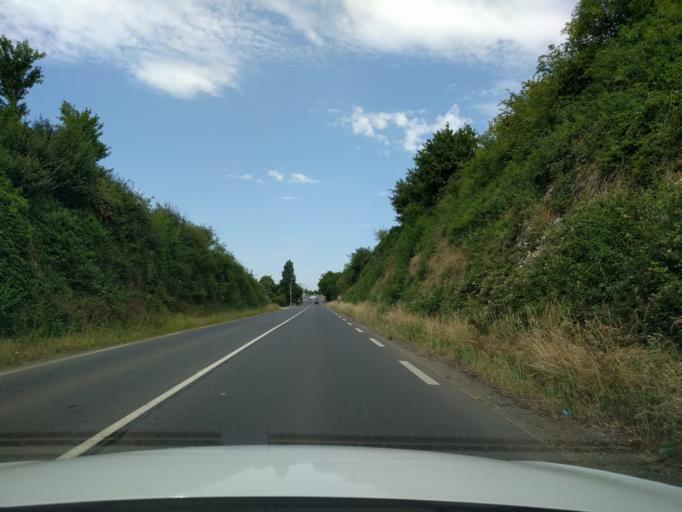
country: FR
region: Poitou-Charentes
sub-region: Departement des Deux-Sevres
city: Bessines
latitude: 46.3460
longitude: -0.5038
